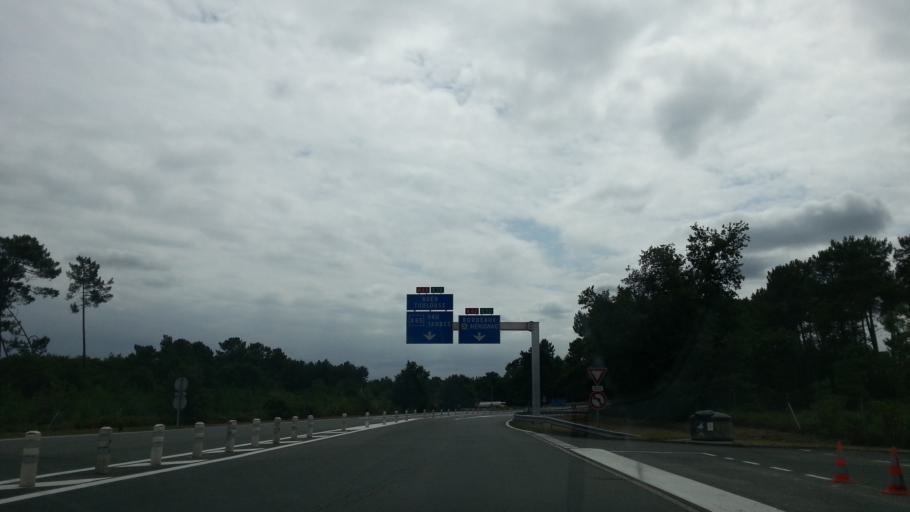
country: FR
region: Aquitaine
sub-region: Departement de la Gironde
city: Illats
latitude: 44.6071
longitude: -0.3671
